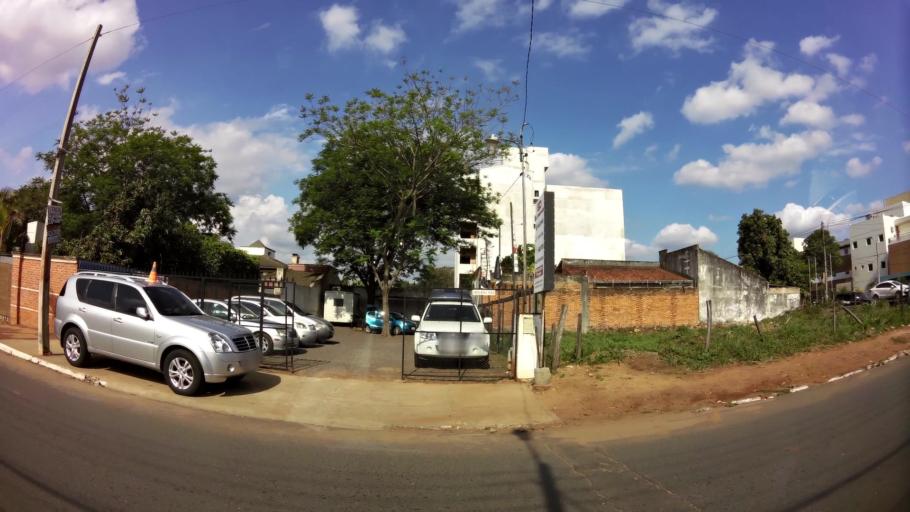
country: PY
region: Central
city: Fernando de la Mora
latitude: -25.3244
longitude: -57.5301
